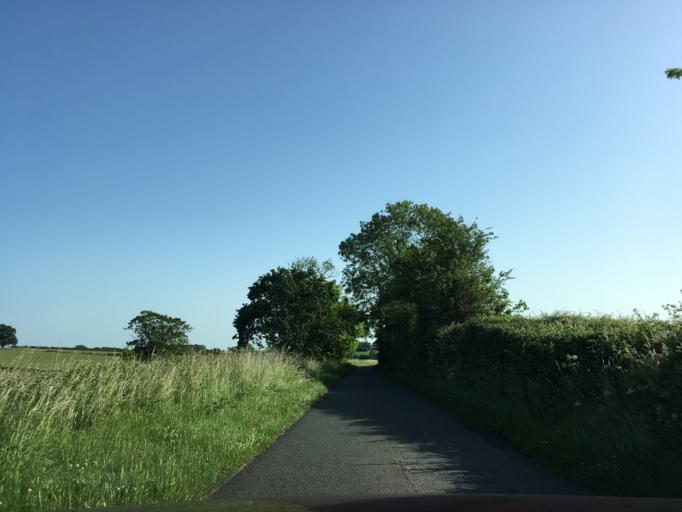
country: GB
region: England
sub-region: Gloucestershire
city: Fairford
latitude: 51.7419
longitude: -1.7319
